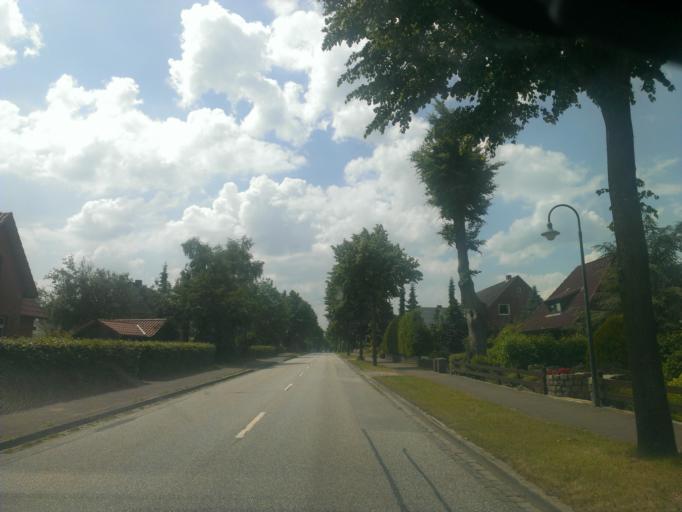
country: DE
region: Schleswig-Holstein
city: Fockbek
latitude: 54.3017
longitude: 9.5974
